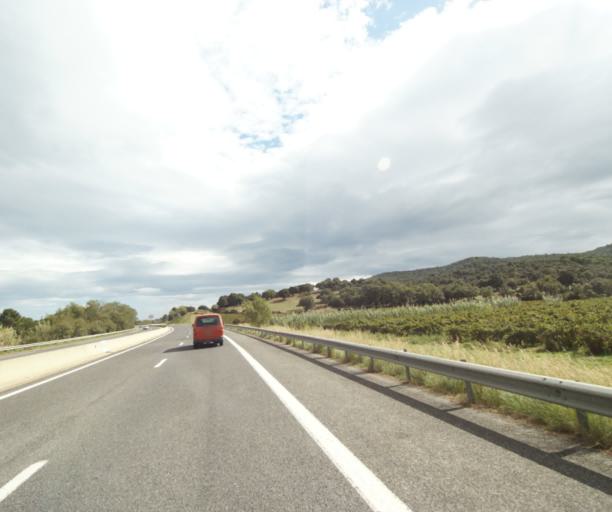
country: FR
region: Languedoc-Roussillon
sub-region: Departement des Pyrenees-Orientales
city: Argelers
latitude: 42.5352
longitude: 3.0356
